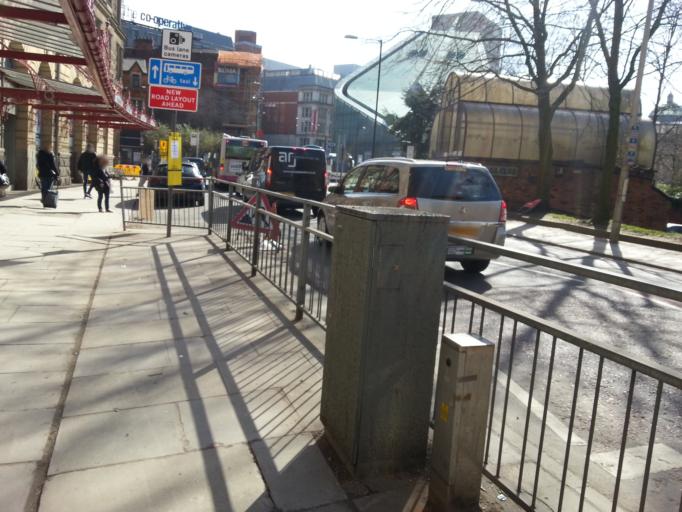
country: GB
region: England
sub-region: Manchester
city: Manchester
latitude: 53.4869
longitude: -2.2425
